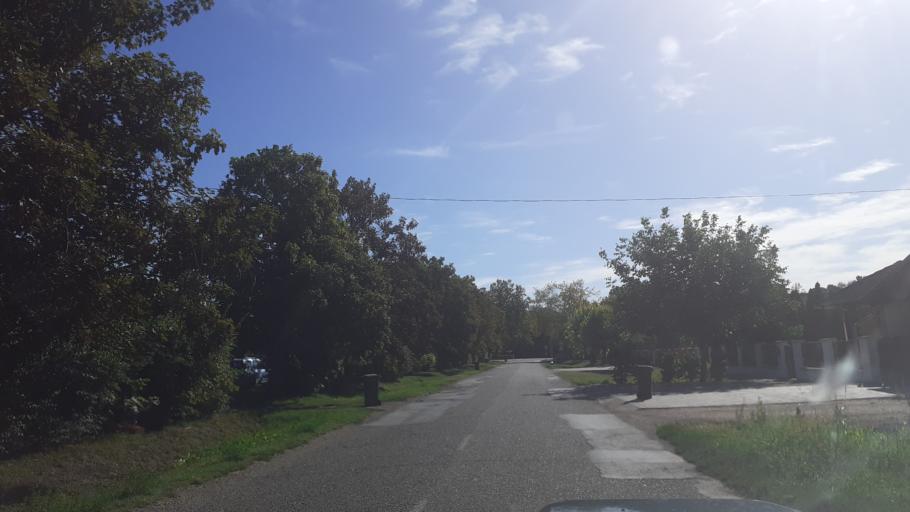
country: HU
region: Fejer
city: Ivancsa
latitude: 47.1913
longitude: 18.7911
